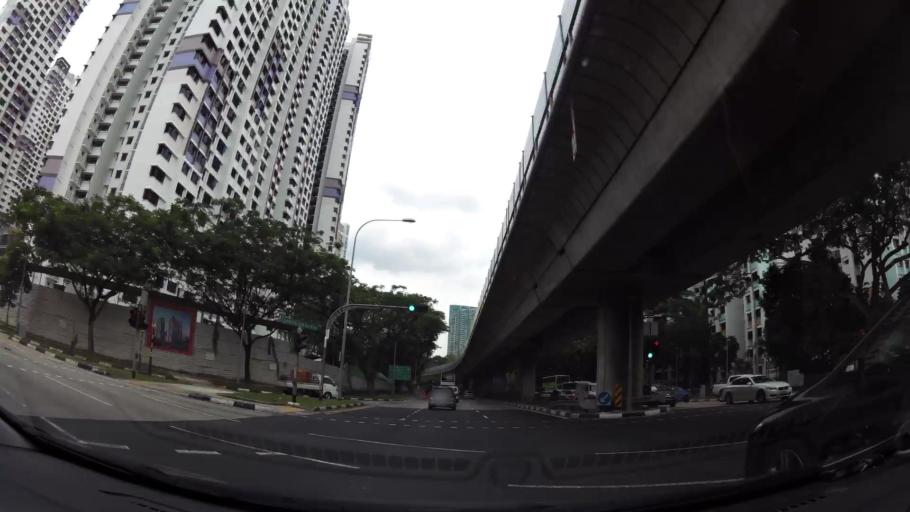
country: SG
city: Singapore
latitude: 1.3089
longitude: 103.7831
